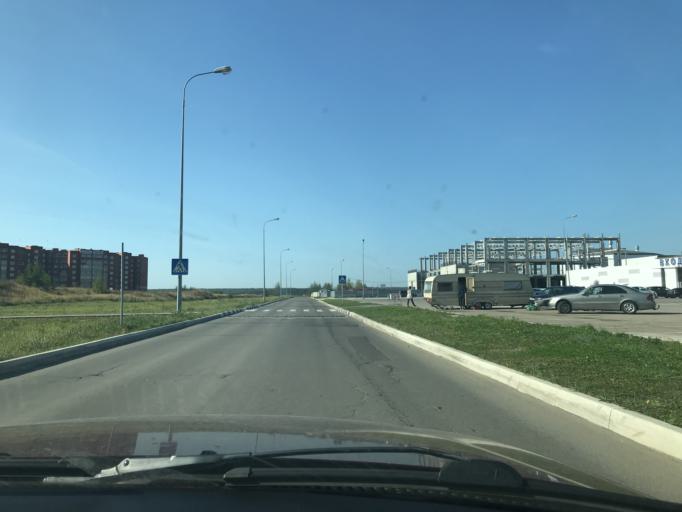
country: RU
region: Kaluga
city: Kaluga
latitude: 54.5851
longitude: 36.2502
